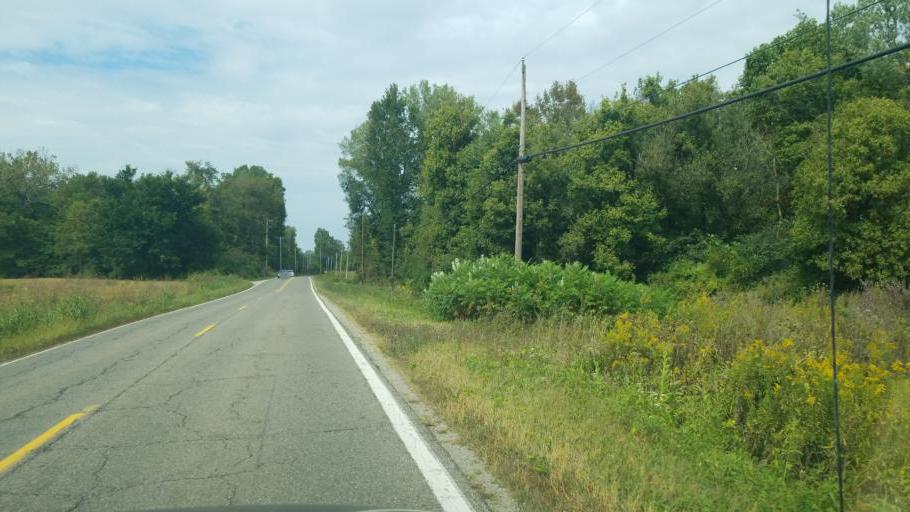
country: US
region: Ohio
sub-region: Licking County
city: Newark
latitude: 40.0636
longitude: -82.2903
